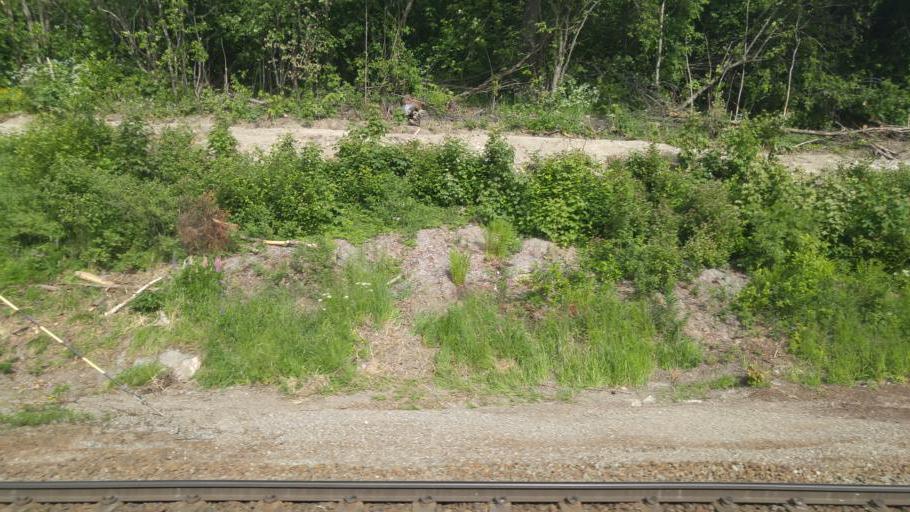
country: NO
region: Sor-Trondelag
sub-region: Trondheim
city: Trondheim
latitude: 63.3914
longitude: 10.3772
